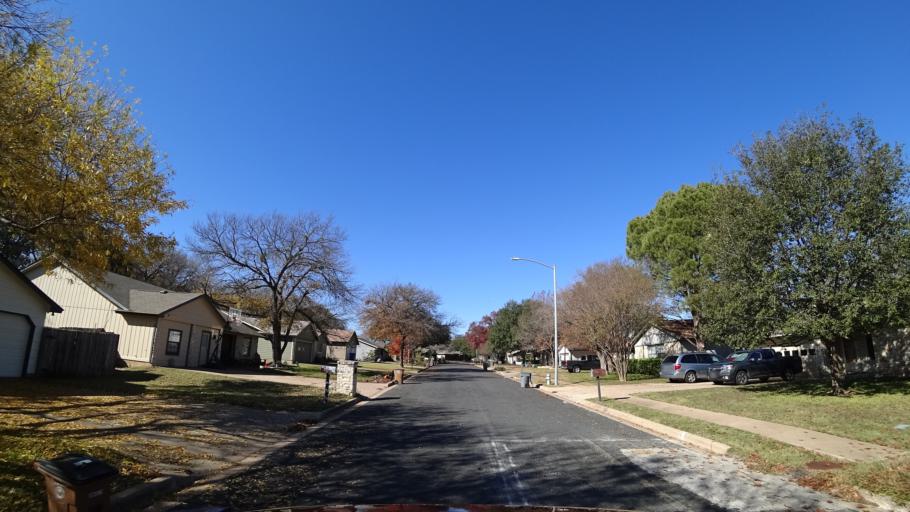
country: US
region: Texas
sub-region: Travis County
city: Wells Branch
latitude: 30.4189
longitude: -97.7152
